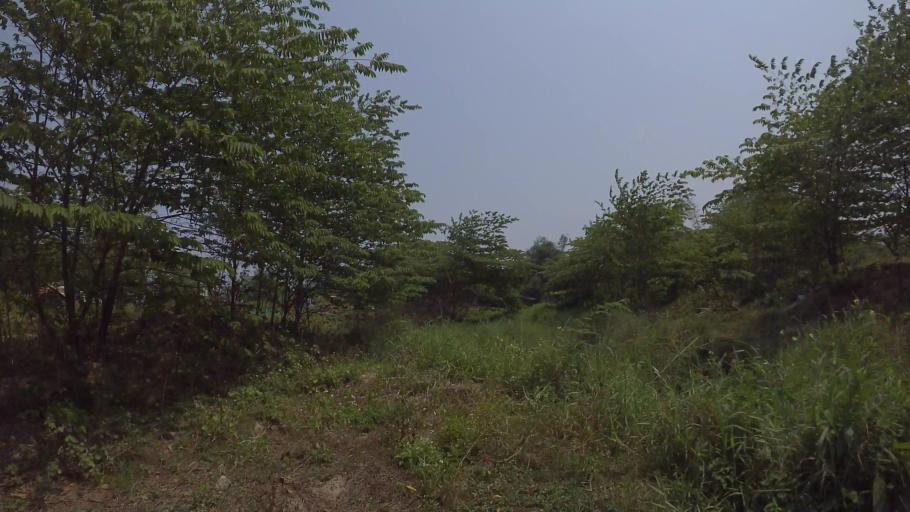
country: VN
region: Da Nang
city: Cam Le
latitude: 16.0192
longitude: 108.2235
